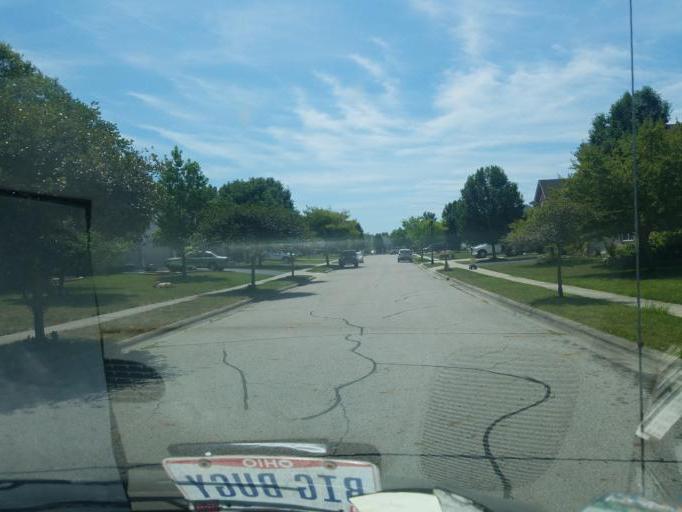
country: US
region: Ohio
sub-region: Franklin County
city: Grove City
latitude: 39.8710
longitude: -83.0963
